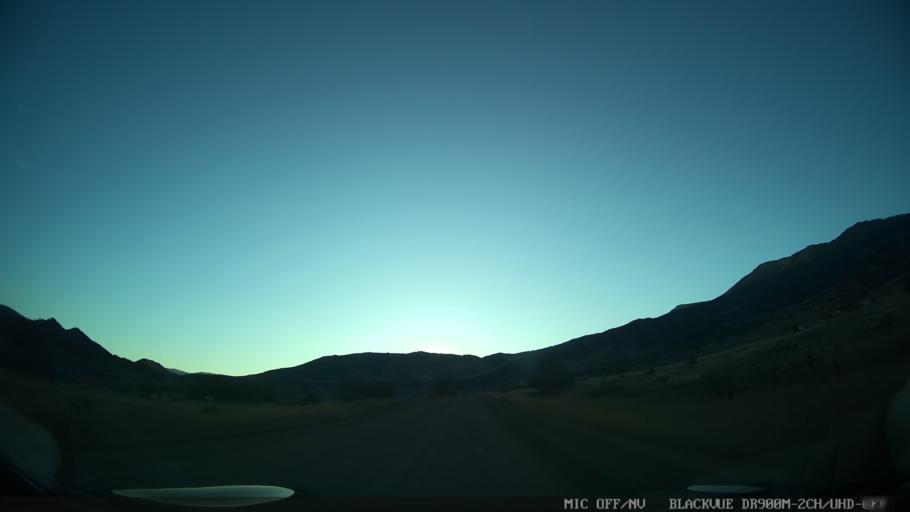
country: US
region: Colorado
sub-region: Eagle County
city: Edwards
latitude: 39.9000
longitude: -106.6018
